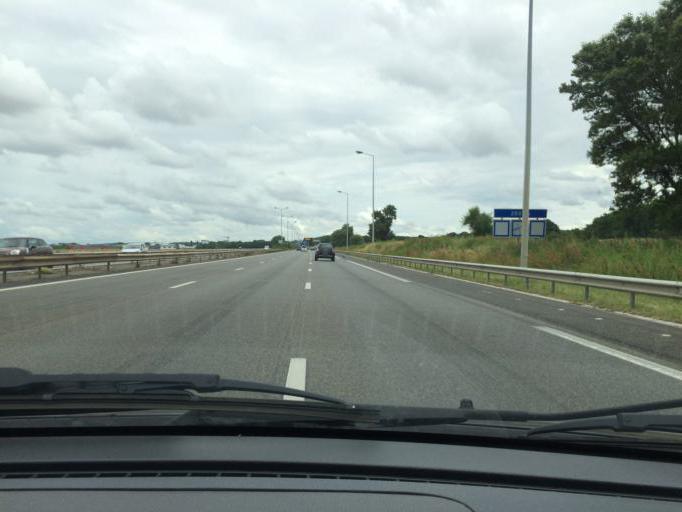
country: FR
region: Rhone-Alpes
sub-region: Departement du Rhone
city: Saint-Priest
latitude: 45.7168
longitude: 4.9407
